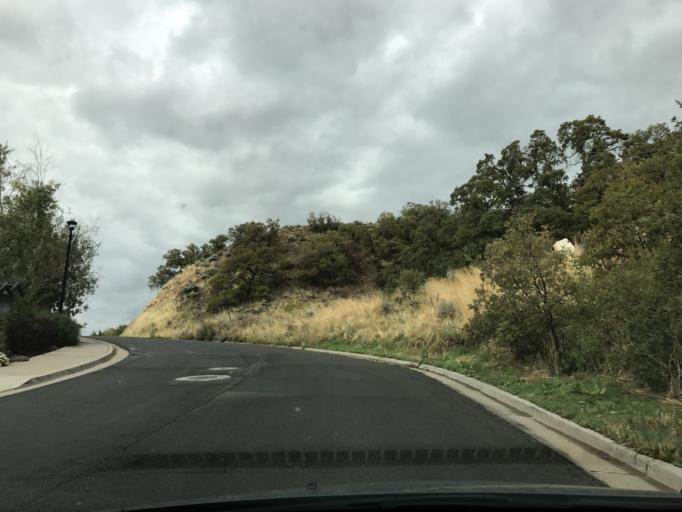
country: US
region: Utah
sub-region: Davis County
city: Fruit Heights
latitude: 41.0196
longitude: -111.8992
